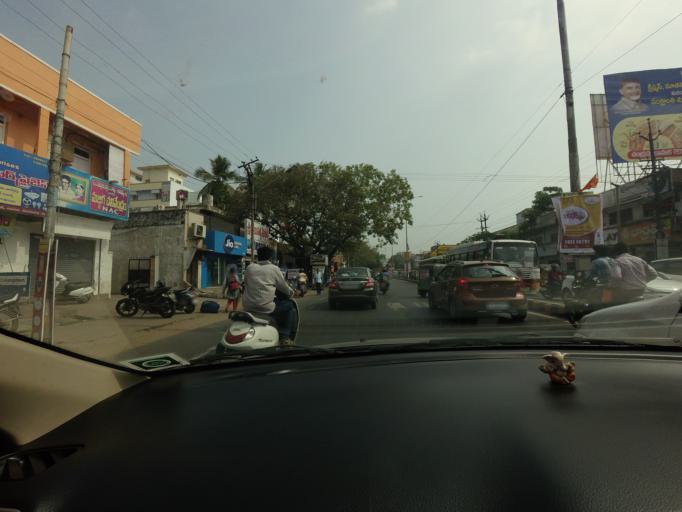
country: IN
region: Andhra Pradesh
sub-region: Krishna
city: Yanamalakuduru
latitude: 16.4949
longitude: 80.6616
